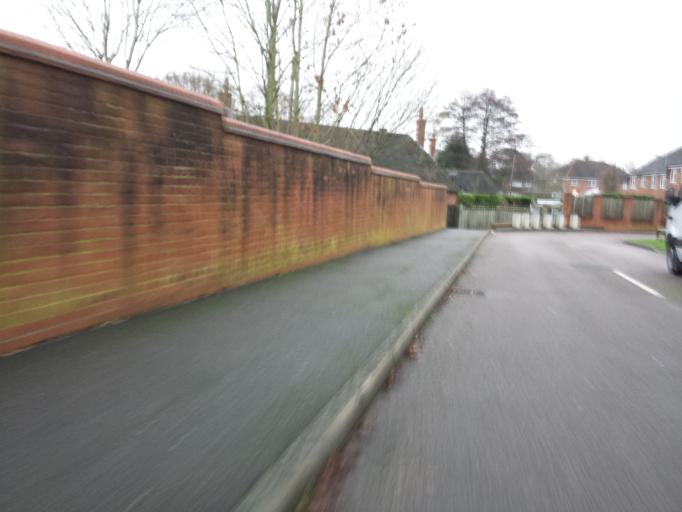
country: GB
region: England
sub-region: Surrey
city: Bagshot
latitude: 51.3601
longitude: -0.6887
